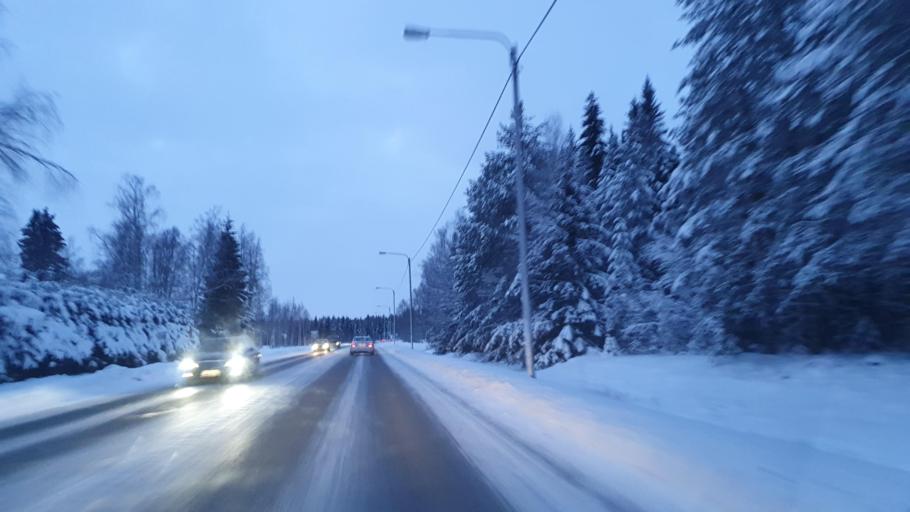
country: FI
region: Northern Ostrobothnia
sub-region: Oulu
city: Tyrnaevae
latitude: 64.9441
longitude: 25.6876
